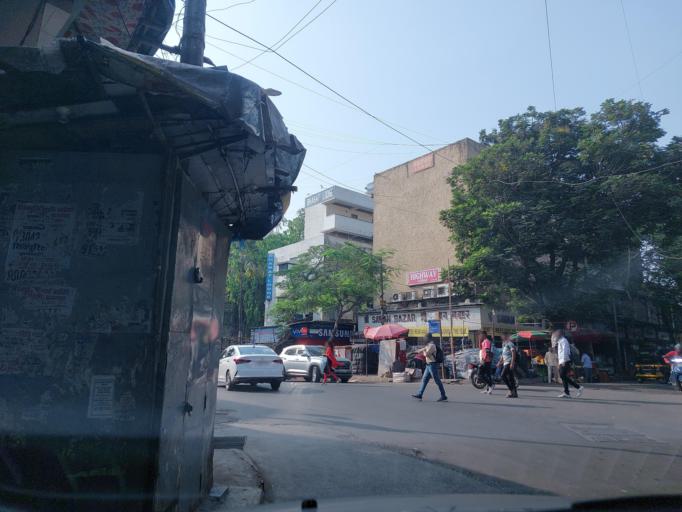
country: IN
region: Maharashtra
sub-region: Mumbai Suburban
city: Mumbai
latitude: 19.0632
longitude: 72.8985
